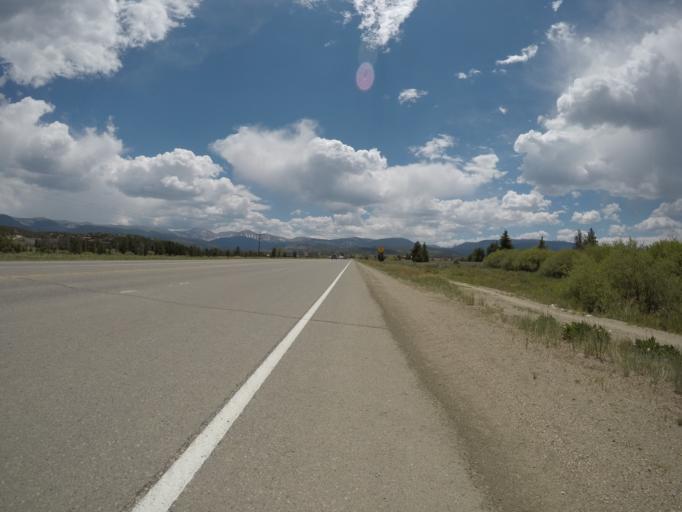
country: US
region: Colorado
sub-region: Grand County
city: Fraser
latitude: 39.9546
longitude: -105.8196
